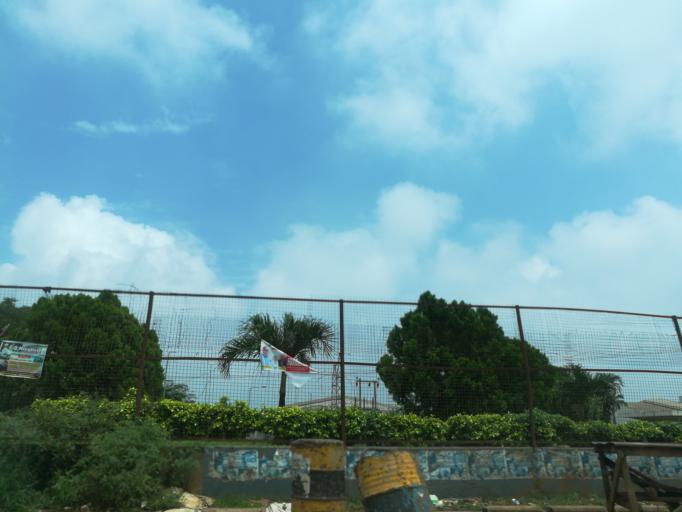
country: NG
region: Lagos
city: Ikorodu
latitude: 6.6749
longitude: 3.5128
